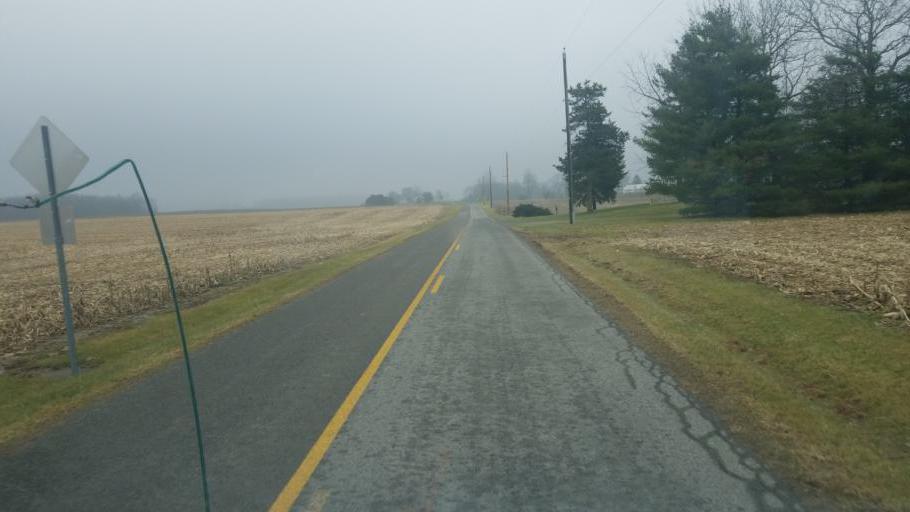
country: US
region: Ohio
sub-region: Hardin County
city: Kenton
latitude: 40.5025
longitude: -83.5355
